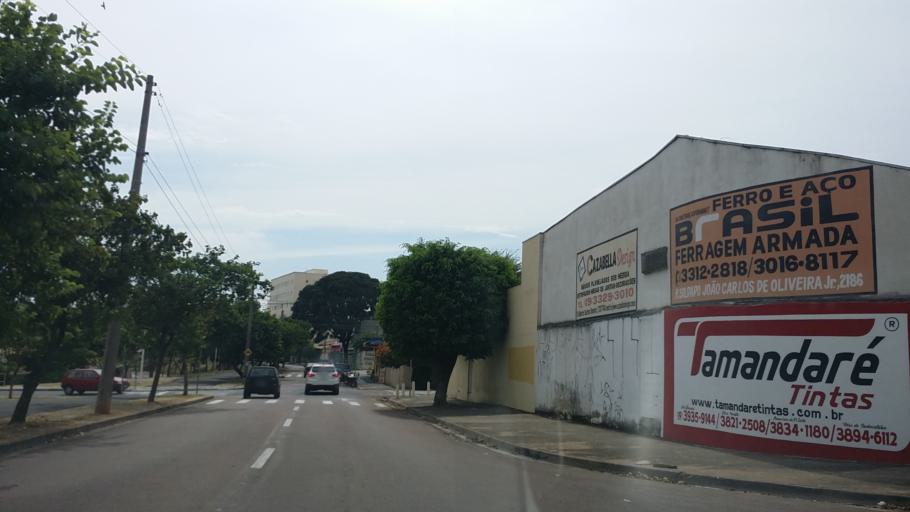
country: BR
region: Sao Paulo
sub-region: Indaiatuba
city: Indaiatuba
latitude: -23.0968
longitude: -47.2218
